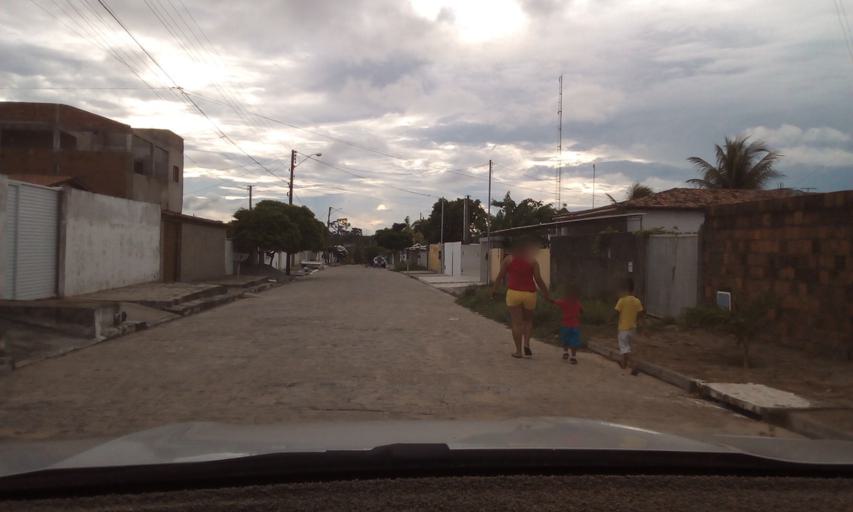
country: BR
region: Paraiba
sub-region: Joao Pessoa
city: Joao Pessoa
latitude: -7.1748
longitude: -34.8196
